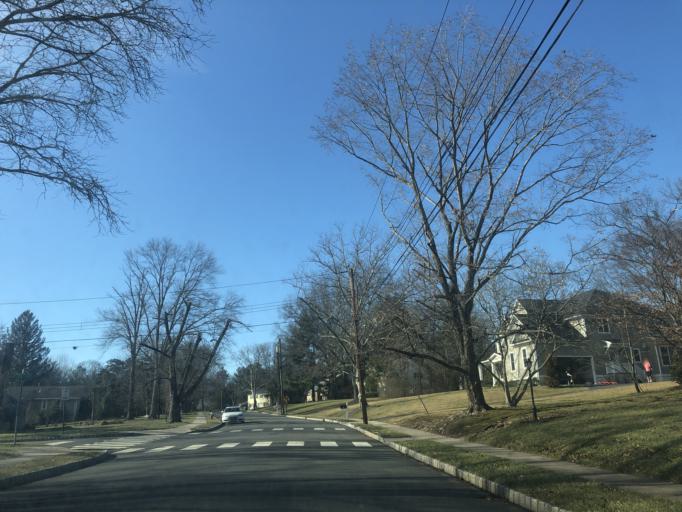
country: US
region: New Jersey
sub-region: Somerset County
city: Kingston
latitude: 40.3705
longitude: -74.6307
